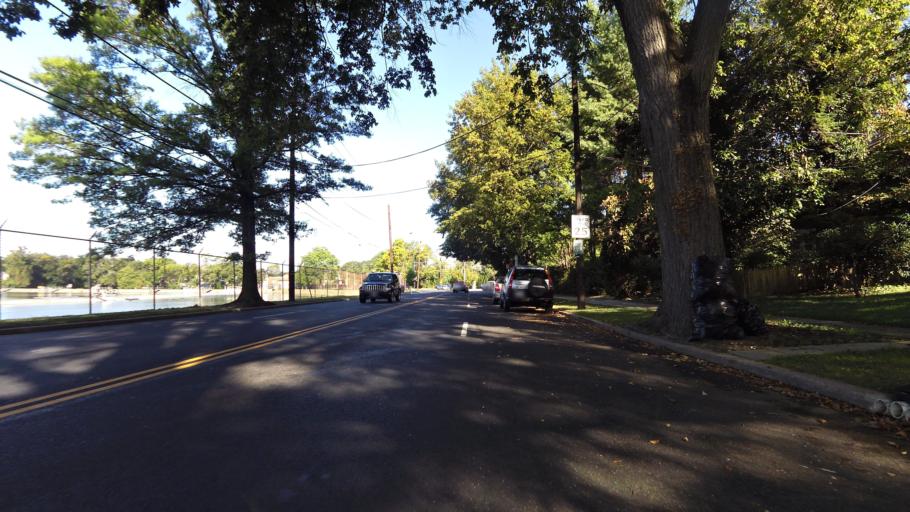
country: US
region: Virginia
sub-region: Arlington County
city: Arlington
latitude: 38.9142
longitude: -77.0925
